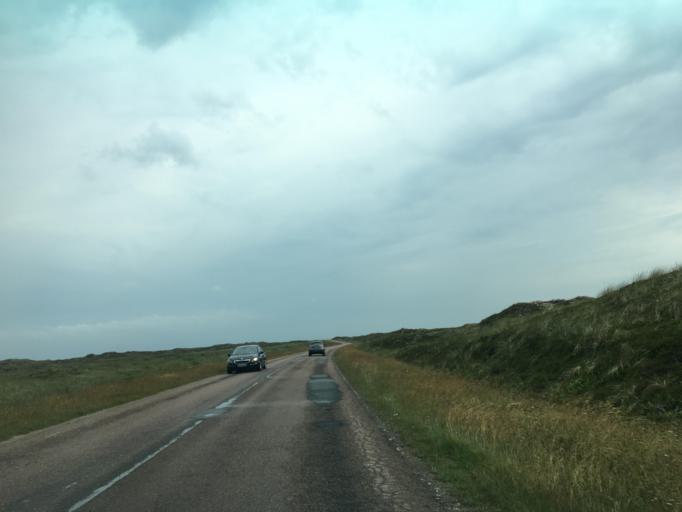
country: DK
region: North Denmark
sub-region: Thisted Kommune
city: Hurup
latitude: 56.9575
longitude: 8.3842
